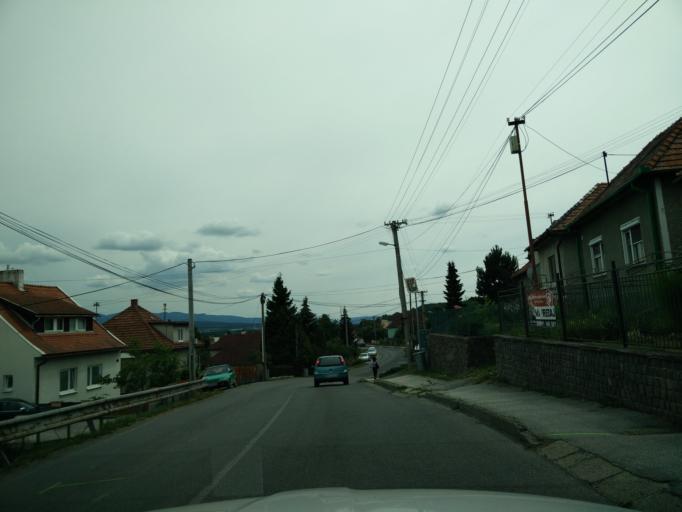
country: SK
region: Nitriansky
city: Bojnice
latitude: 48.7686
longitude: 18.5741
